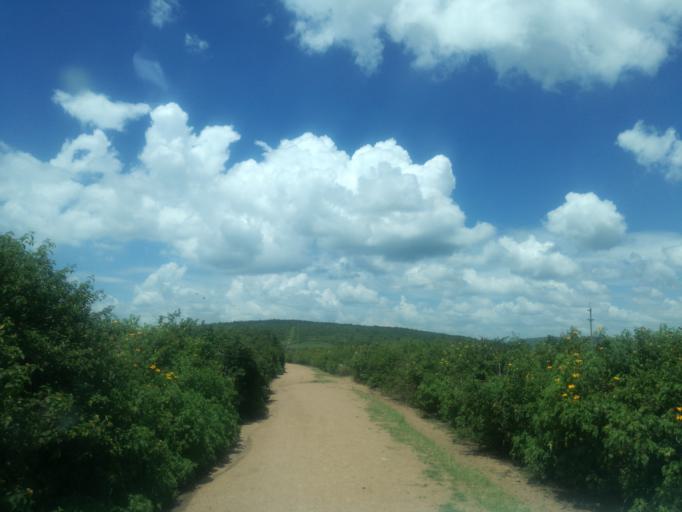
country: TZ
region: Mara
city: Mugumu
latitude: -1.7778
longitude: 34.5994
